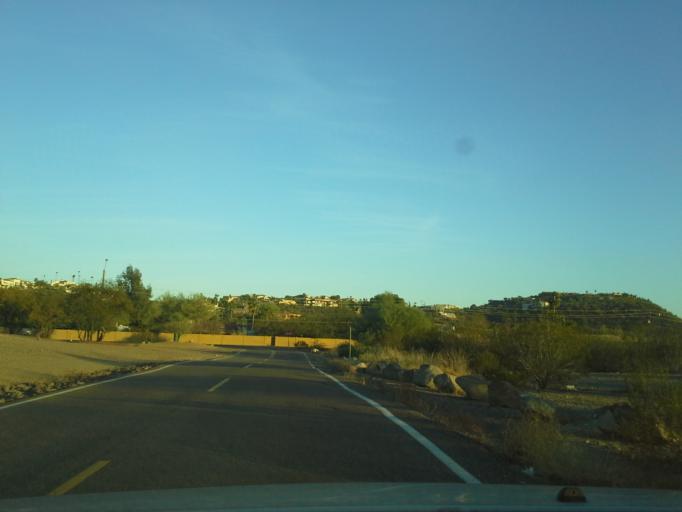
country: US
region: Arizona
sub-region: Maricopa County
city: Glendale
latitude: 33.6212
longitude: -112.1010
